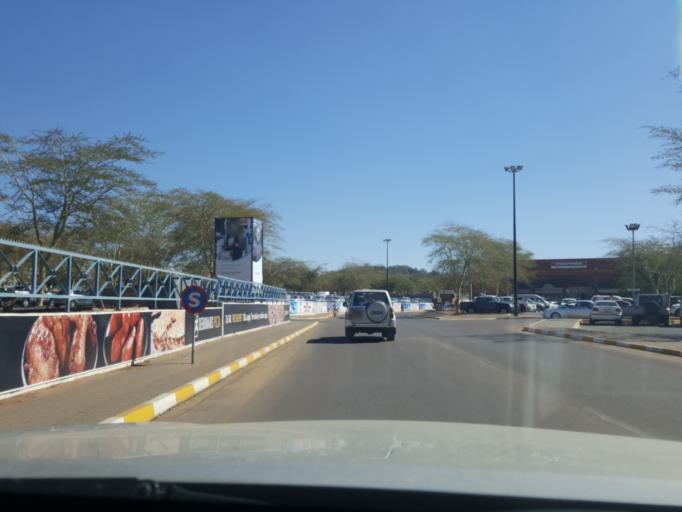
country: BW
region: South East
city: Gaborone
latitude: -24.6882
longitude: 25.8798
